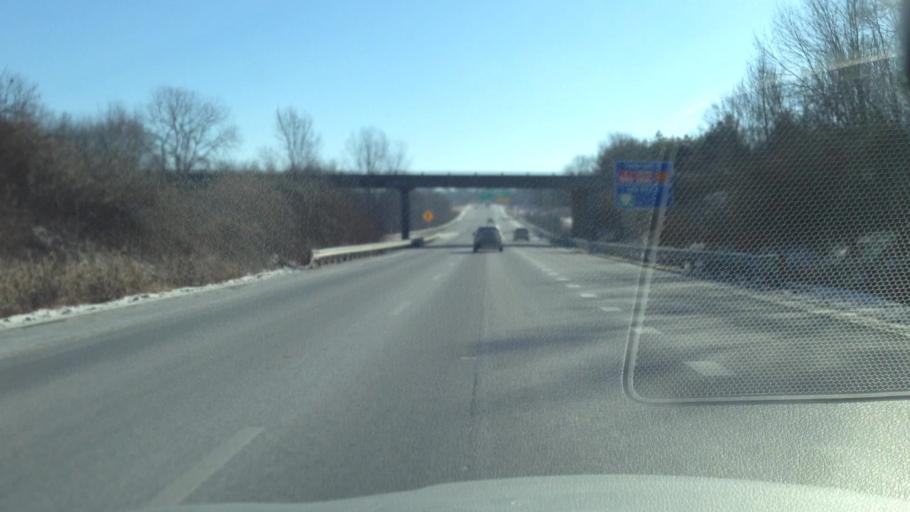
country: US
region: Missouri
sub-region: Platte County
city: Riverside
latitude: 39.1832
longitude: -94.5927
